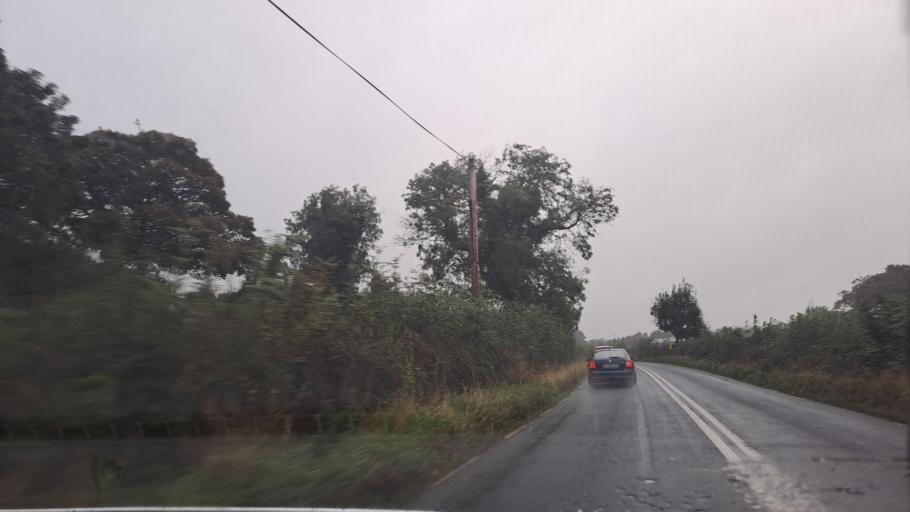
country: IE
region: Leinster
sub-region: Lu
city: Dundalk
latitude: 53.9784
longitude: -6.5175
